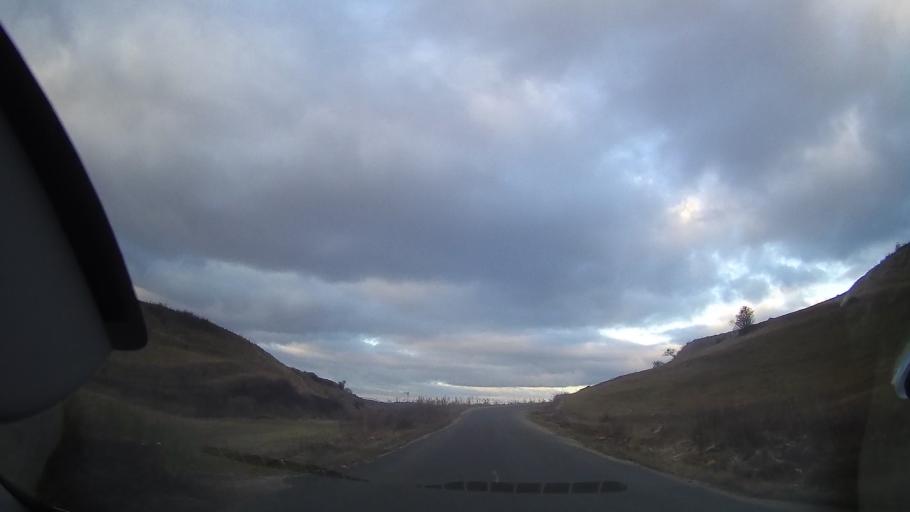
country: RO
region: Cluj
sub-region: Comuna Calatele
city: Calatele
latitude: 46.7816
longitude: 23.0470
